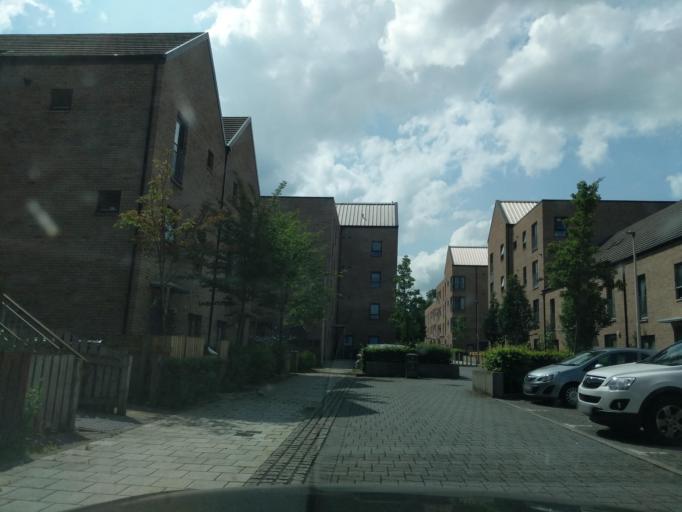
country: GB
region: Scotland
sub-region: Midlothian
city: Loanhead
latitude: 55.9061
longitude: -3.1544
